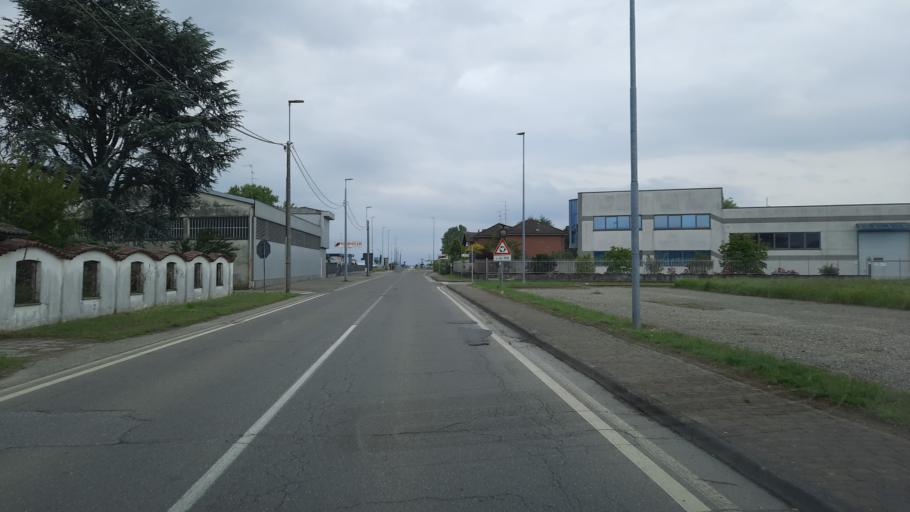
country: IT
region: Lombardy
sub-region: Provincia di Pavia
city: Robbio
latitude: 45.2828
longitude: 8.6007
